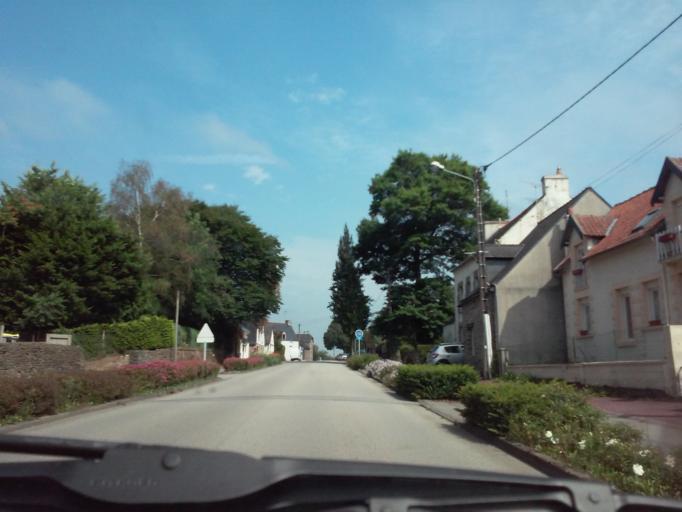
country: FR
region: Brittany
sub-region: Departement du Morbihan
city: Ploermel
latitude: 47.9259
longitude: -2.4008
